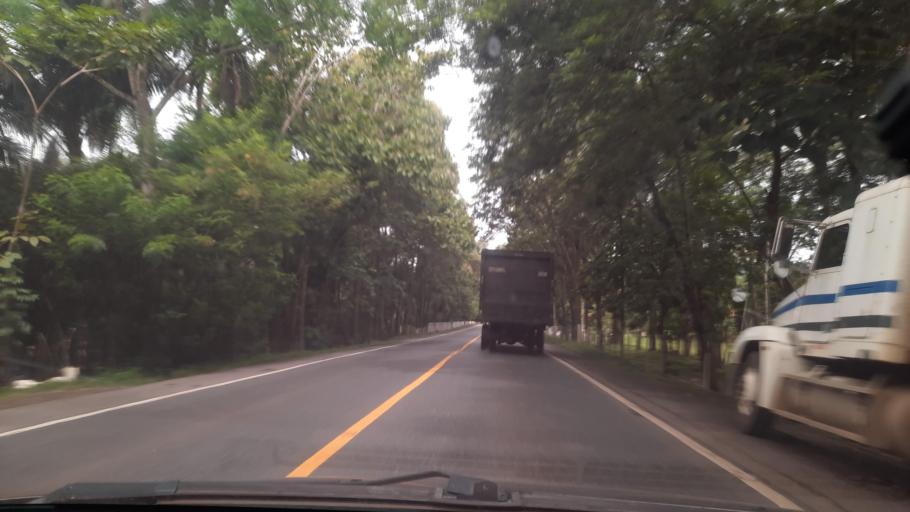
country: GT
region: Izabal
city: Morales
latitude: 15.4639
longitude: -88.9188
